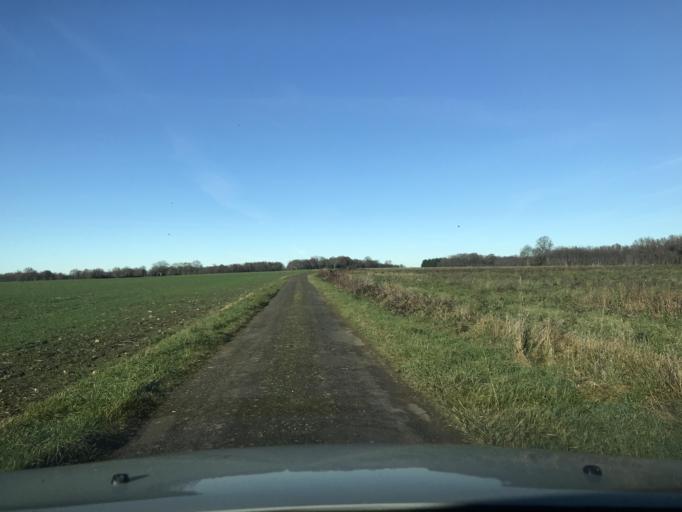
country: FR
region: Poitou-Charentes
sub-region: Departement de la Charente
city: Saint-Claud
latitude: 45.8545
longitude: 0.4970
